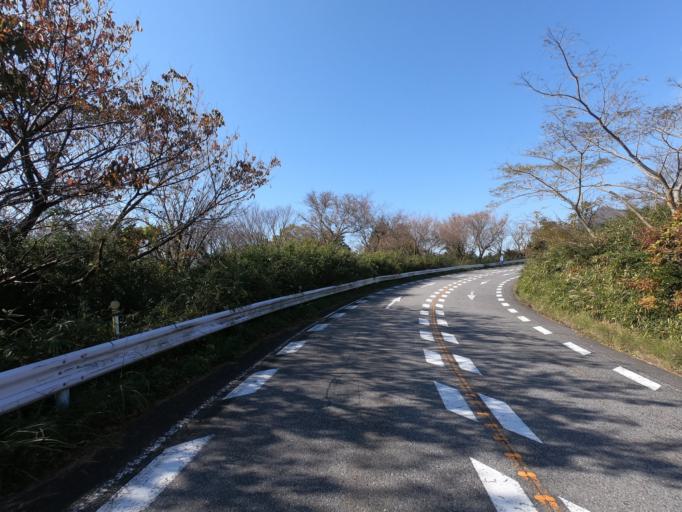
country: JP
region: Ibaraki
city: Tsukuba
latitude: 36.2088
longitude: 140.1235
